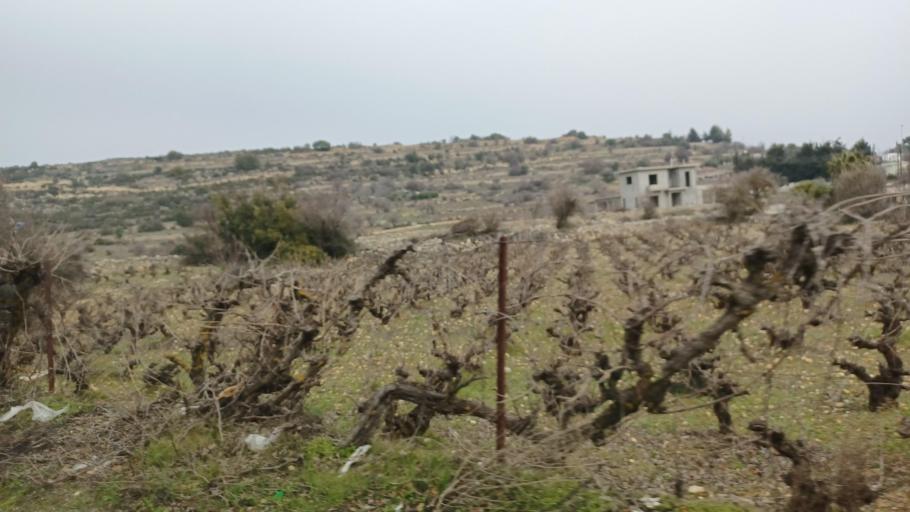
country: CY
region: Limassol
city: Pachna
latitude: 34.7779
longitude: 32.7877
